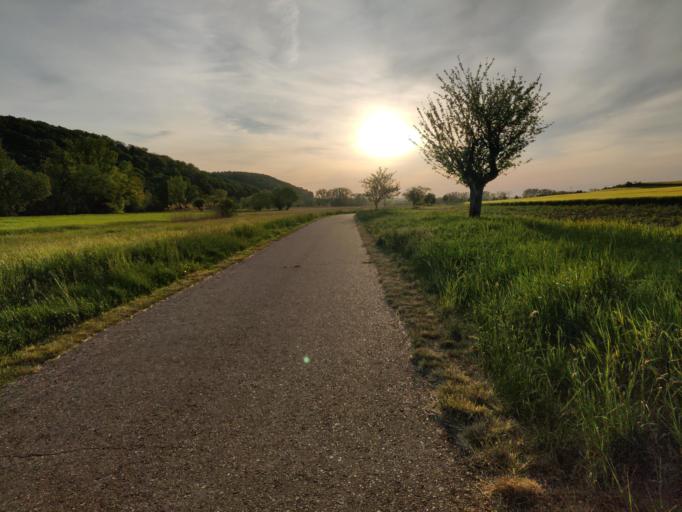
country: DE
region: Saxony-Anhalt
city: Balgstadt
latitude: 51.2134
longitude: 11.7166
